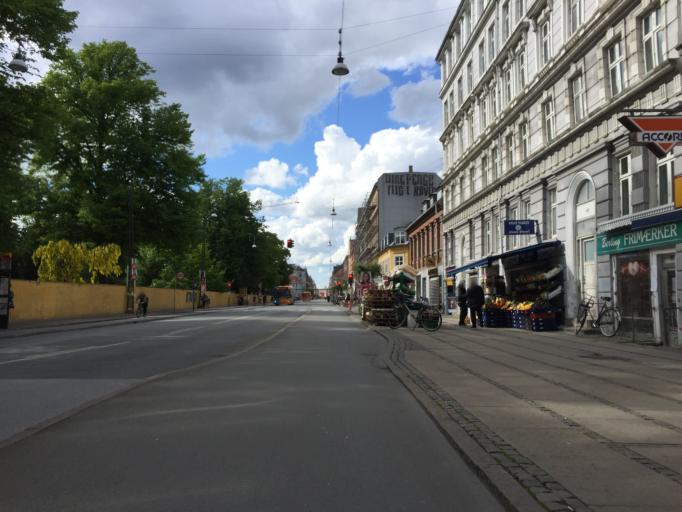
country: DK
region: Capital Region
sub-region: Kobenhavn
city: Copenhagen
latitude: 55.6922
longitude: 12.5520
